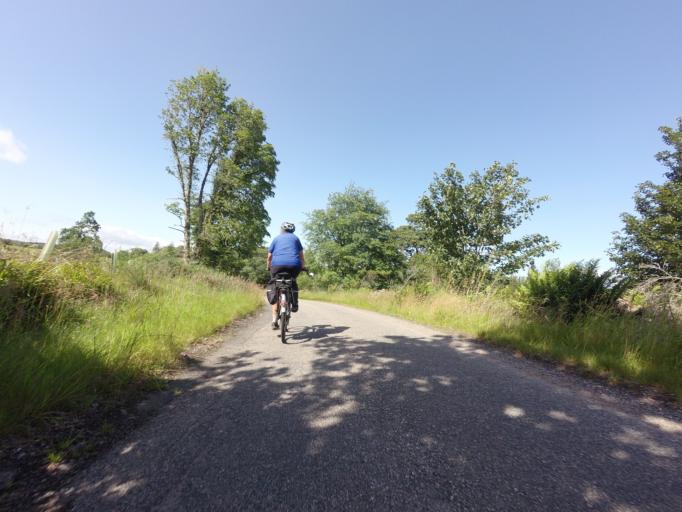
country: GB
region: Scotland
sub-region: Highland
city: Nairn
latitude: 57.5047
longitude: -3.9369
